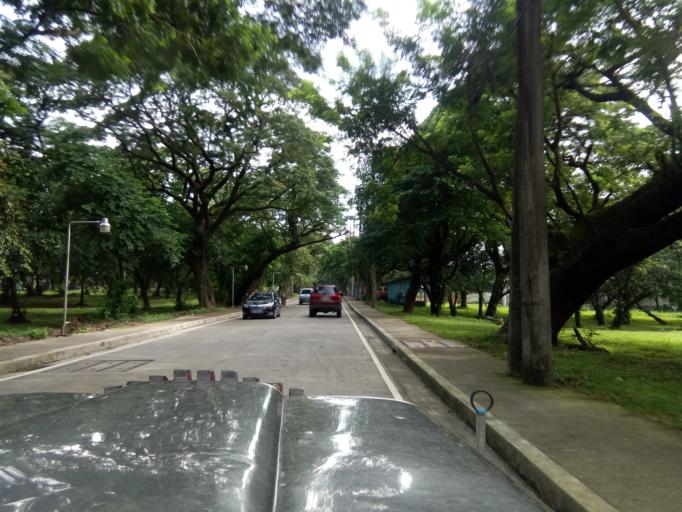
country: PH
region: Metro Manila
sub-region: Quezon City
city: Quezon City
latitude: 14.6542
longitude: 121.0623
